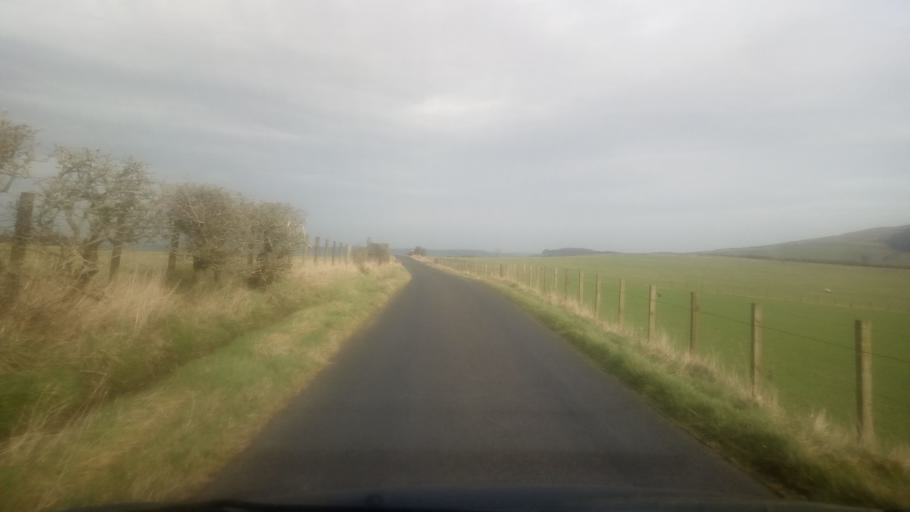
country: GB
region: Scotland
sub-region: The Scottish Borders
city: Hawick
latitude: 55.4178
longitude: -2.7044
